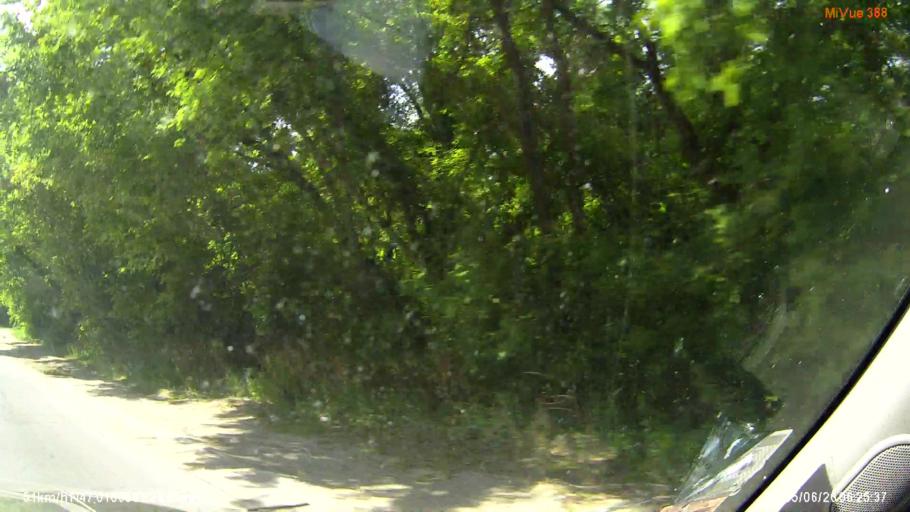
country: MD
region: Chisinau
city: Chisinau
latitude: 47.0108
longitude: 28.8740
